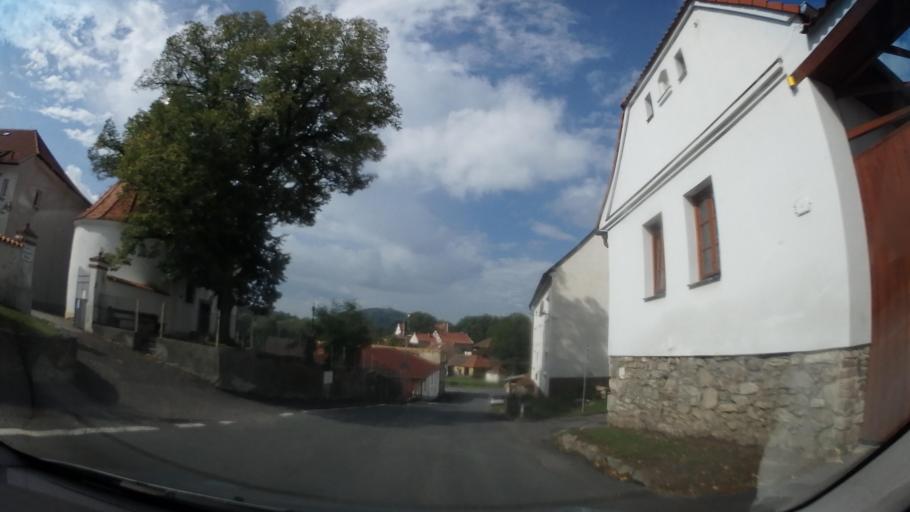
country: CZ
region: Plzensky
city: Horazd'ovice
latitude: 49.2673
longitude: 13.6294
